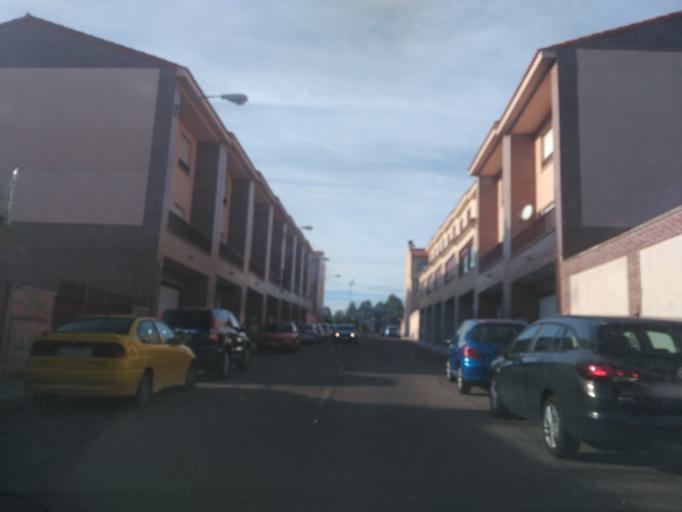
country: ES
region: Castille and Leon
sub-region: Provincia de Salamanca
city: Salamanca
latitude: 40.9762
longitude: -5.6468
